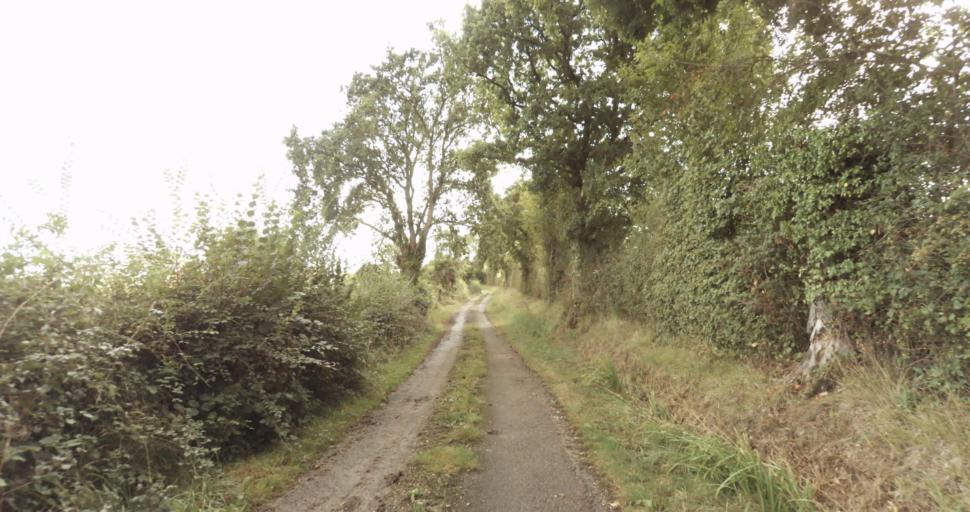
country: FR
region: Lower Normandy
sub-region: Departement de l'Orne
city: Vimoutiers
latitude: 48.8834
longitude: 0.1761
